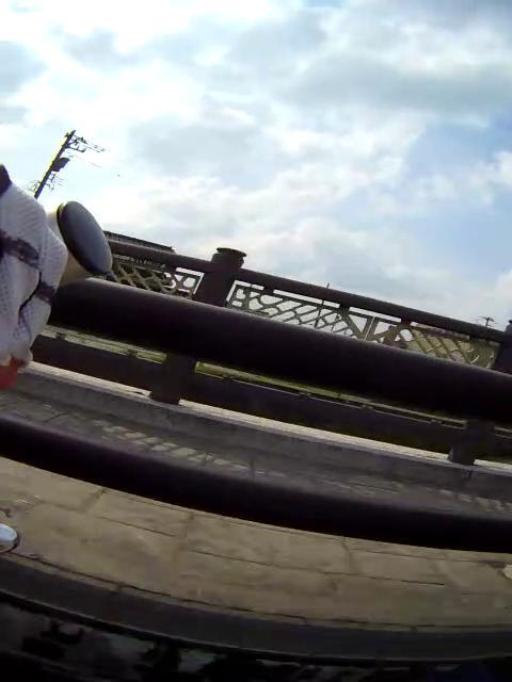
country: JP
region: Toyama
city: Takaoka
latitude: 36.7314
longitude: 137.0020
